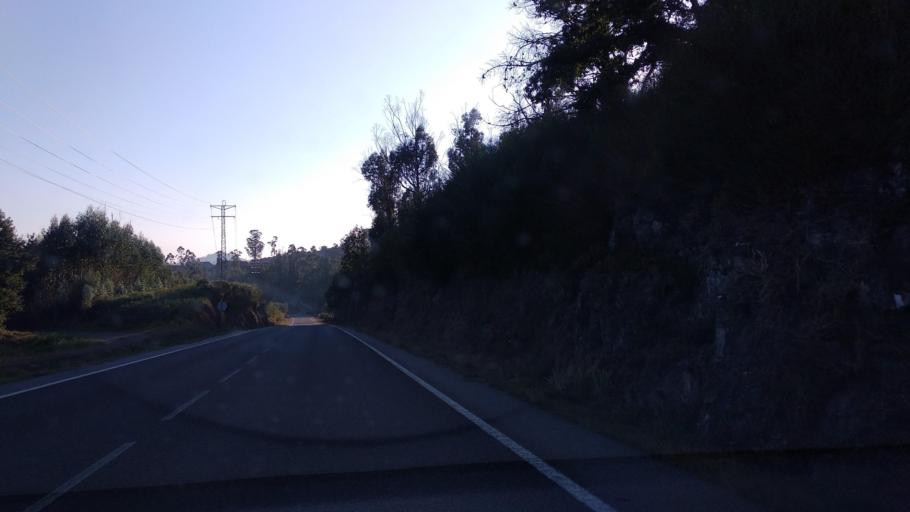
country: ES
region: Galicia
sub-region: Provincia de Pontevedra
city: Ponte Caldelas
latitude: 42.3619
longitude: -8.5366
